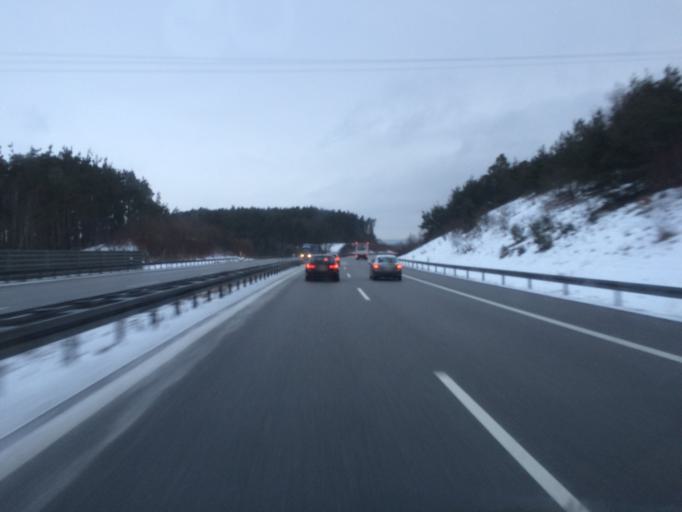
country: DE
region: Bavaria
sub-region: Upper Palatinate
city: Maxhutte-Haidhof
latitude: 49.2013
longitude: 12.1153
